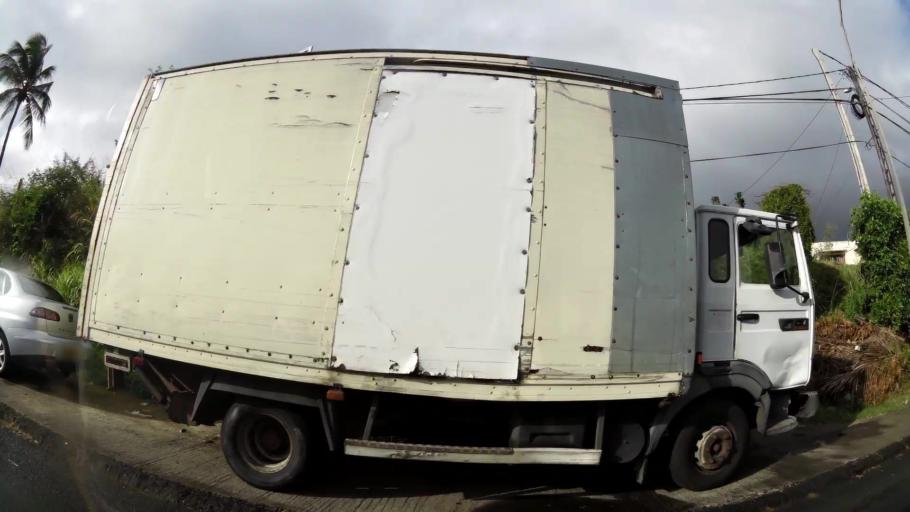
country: MQ
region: Martinique
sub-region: Martinique
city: Le Lamentin
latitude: 14.6192
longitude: -61.0407
